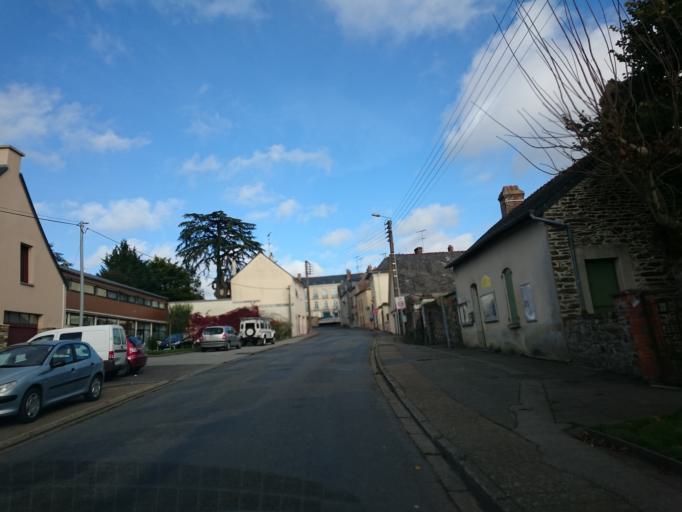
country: FR
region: Brittany
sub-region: Departement d'Ille-et-Vilaine
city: Bain-de-Bretagne
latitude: 47.8403
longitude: -1.6802
